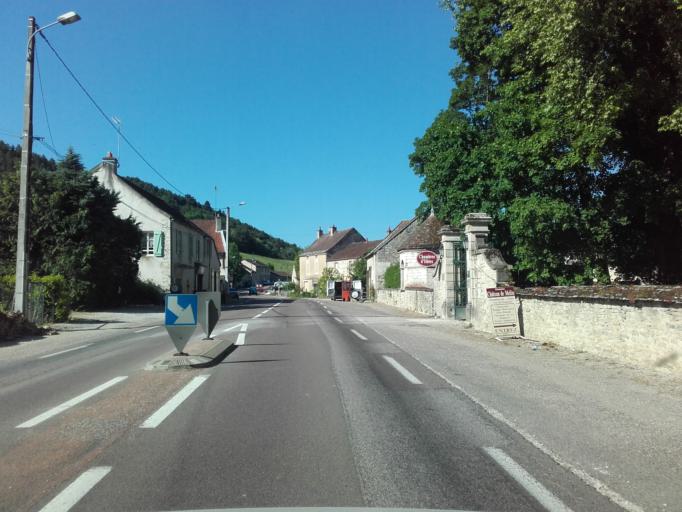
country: FR
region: Bourgogne
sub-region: Departement de la Cote-d'Or
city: Meursault
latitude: 46.9814
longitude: 4.7110
